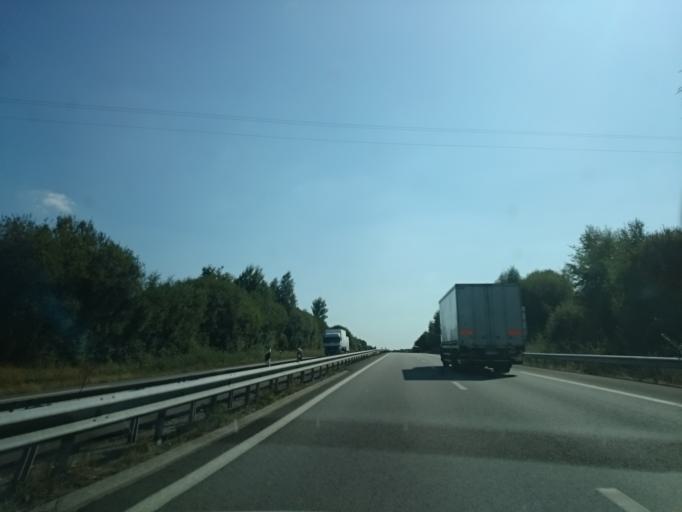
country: FR
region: Brittany
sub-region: Departement d'Ille-et-Vilaine
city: La Dominelais
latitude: 47.7533
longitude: -1.7150
